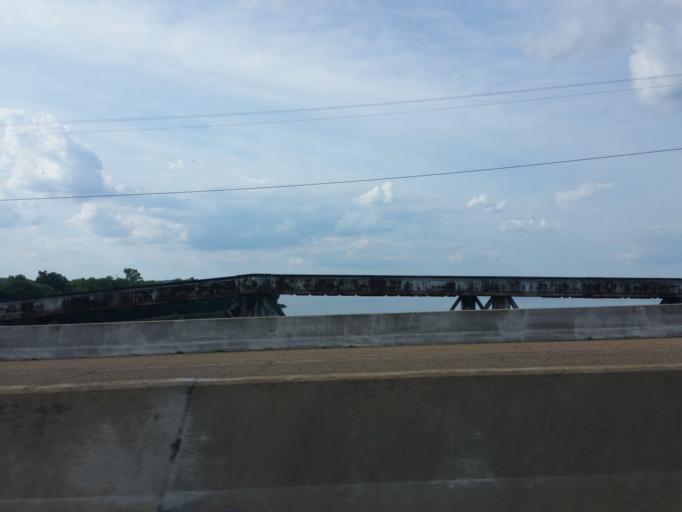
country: US
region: Tennessee
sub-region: Humphreys County
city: New Johnsonville
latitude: 36.0172
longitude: -88.0027
